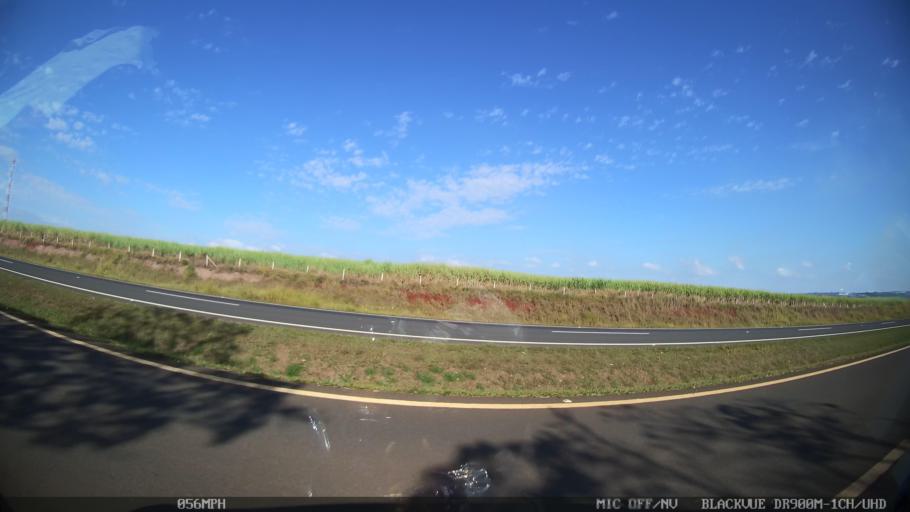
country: BR
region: Sao Paulo
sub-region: Iracemapolis
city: Iracemapolis
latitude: -22.6710
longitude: -47.5551
